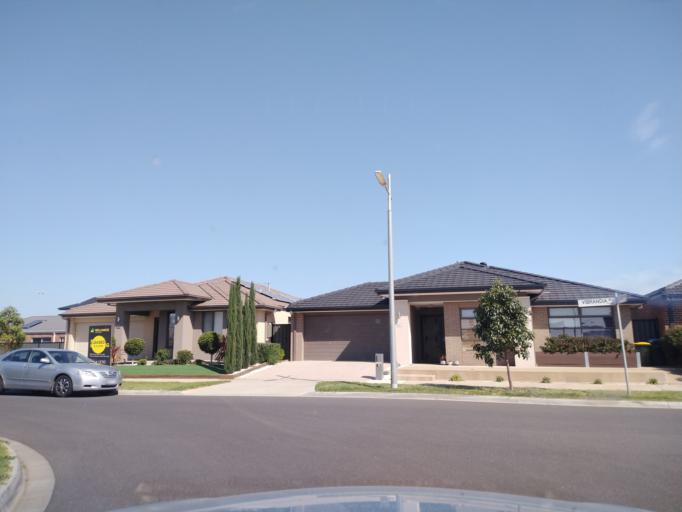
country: AU
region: Victoria
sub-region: Wyndham
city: Williams Landing
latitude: -37.8396
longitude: 144.7333
